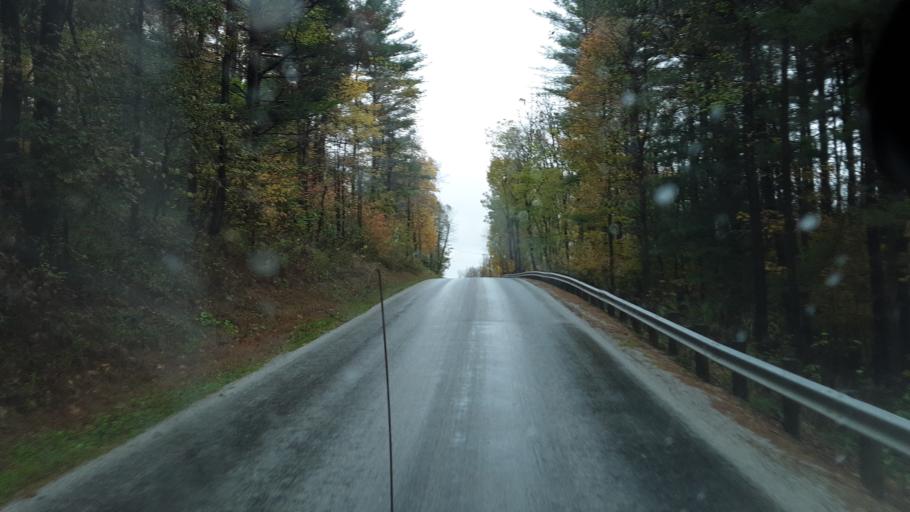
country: US
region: Ohio
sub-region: Coshocton County
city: West Lafayette
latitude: 40.3948
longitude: -81.7630
